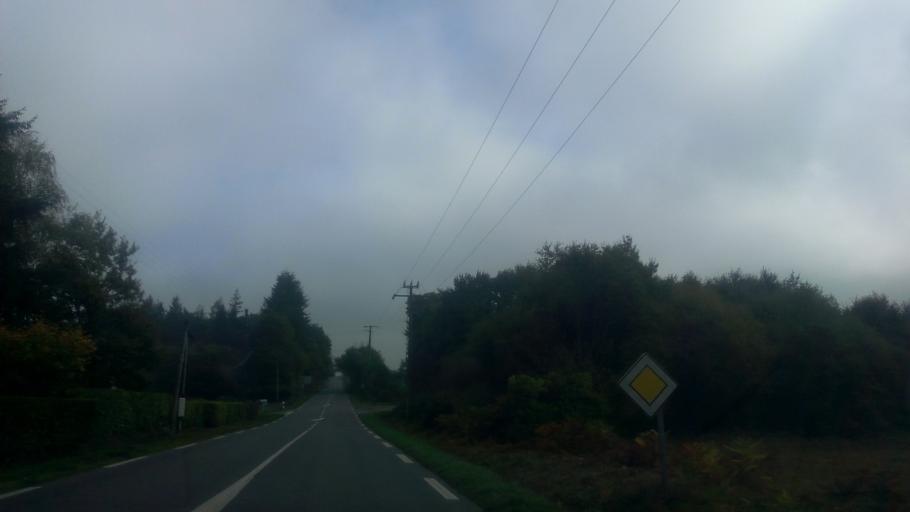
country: FR
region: Pays de la Loire
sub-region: Departement de la Loire-Atlantique
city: Avessac
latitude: 47.6361
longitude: -1.9582
